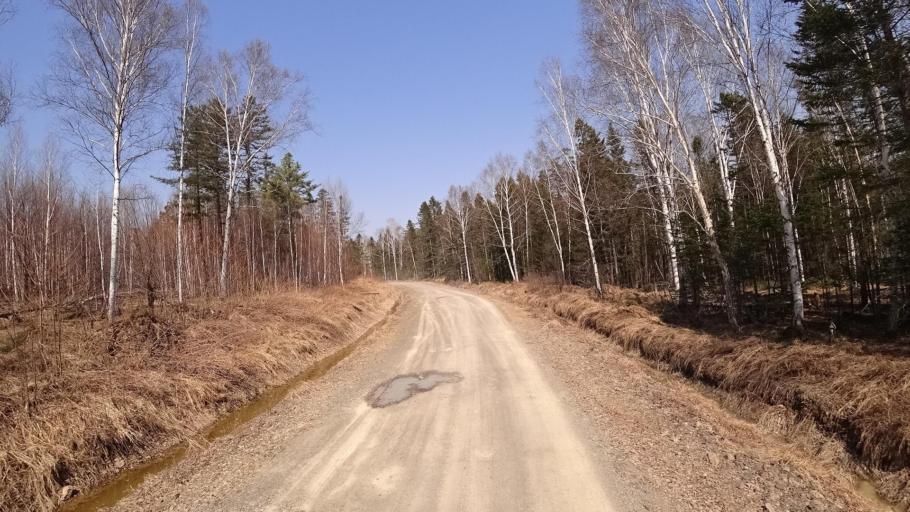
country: RU
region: Khabarovsk Krai
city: Selikhino
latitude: 50.6266
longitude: 137.4050
